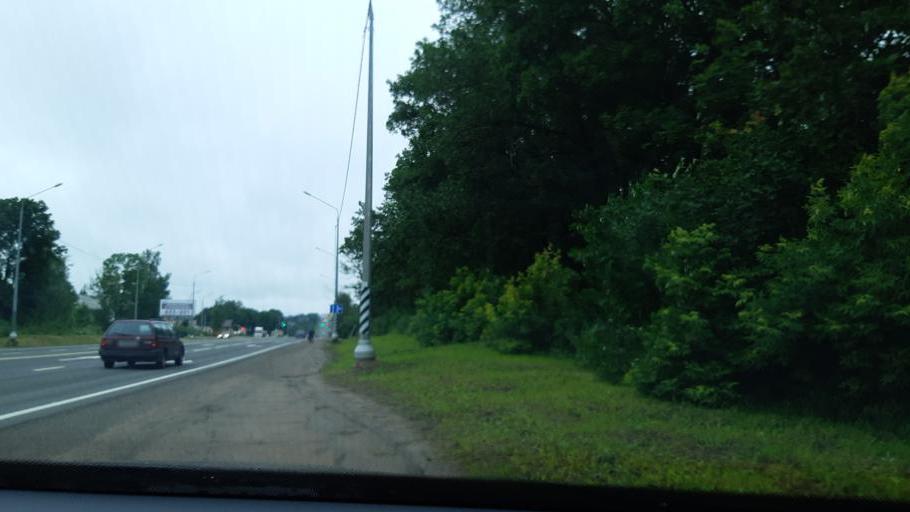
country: RU
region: Smolensk
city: Smolensk
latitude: 54.7178
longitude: 32.1068
